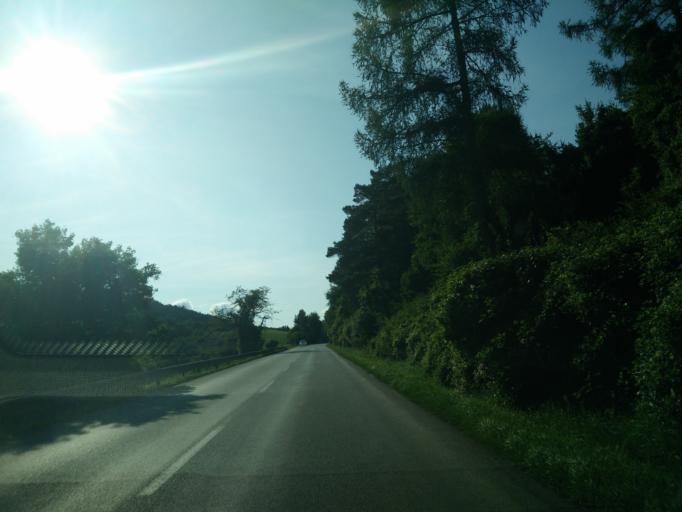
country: SK
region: Nitriansky
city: Prievidza
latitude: 48.8832
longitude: 18.7115
